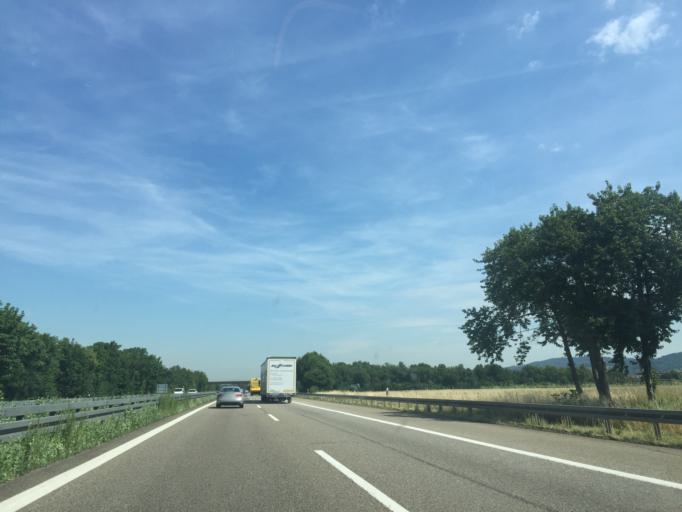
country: DE
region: Baden-Wuerttemberg
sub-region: Karlsruhe Region
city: Schriesheim
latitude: 49.4874
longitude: 8.6388
